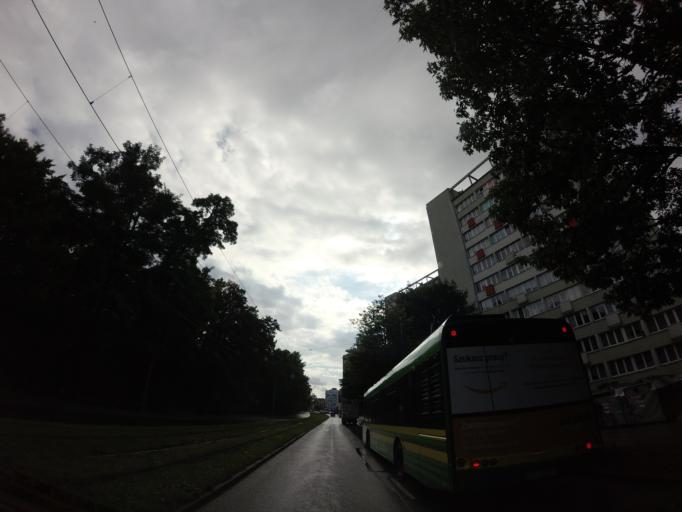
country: PL
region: West Pomeranian Voivodeship
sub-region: Szczecin
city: Szczecin
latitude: 53.4338
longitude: 14.5593
